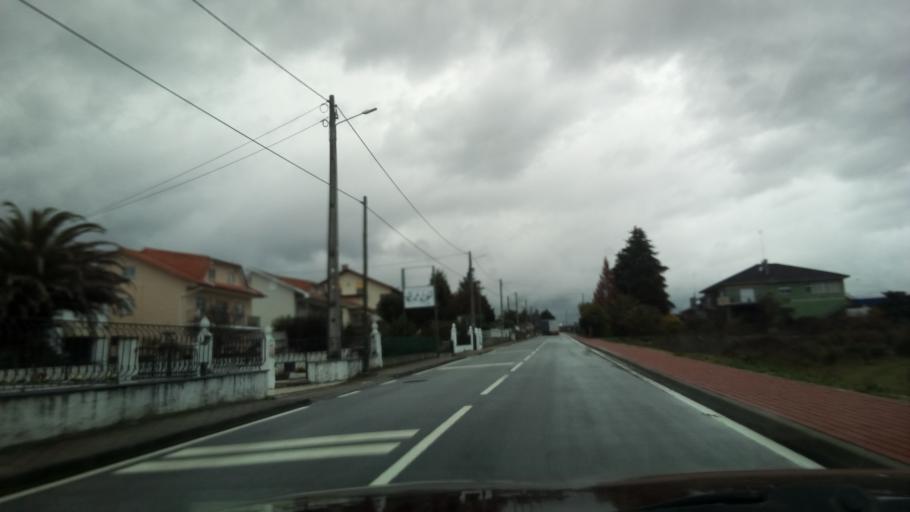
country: PT
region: Guarda
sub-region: Celorico da Beira
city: Celorico da Beira
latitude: 40.6292
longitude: -7.3421
